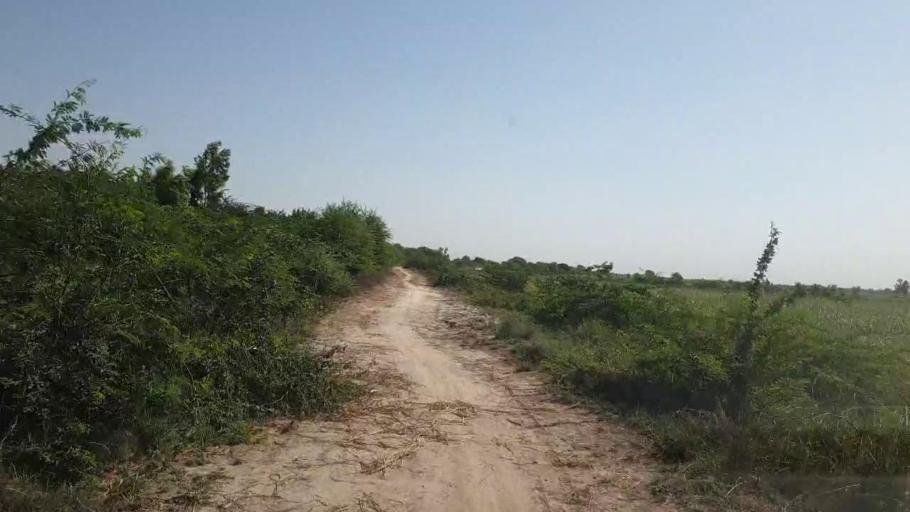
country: PK
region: Sindh
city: Kadhan
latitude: 24.6051
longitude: 69.0027
